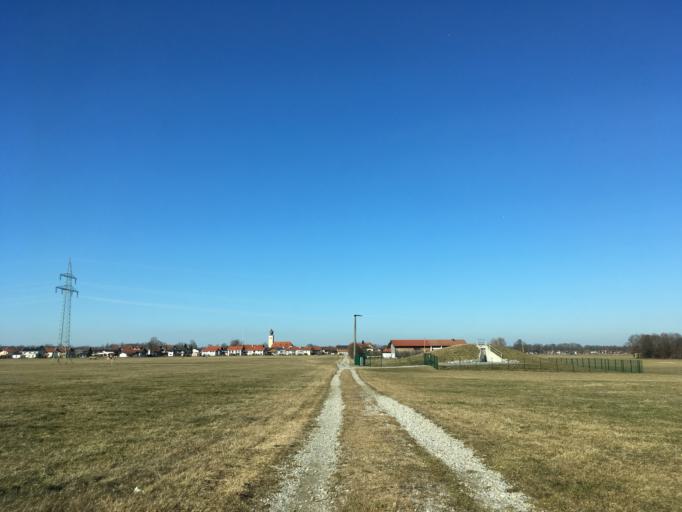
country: DE
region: Bavaria
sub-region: Upper Bavaria
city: Irschenberg
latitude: 47.8563
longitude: 11.9454
